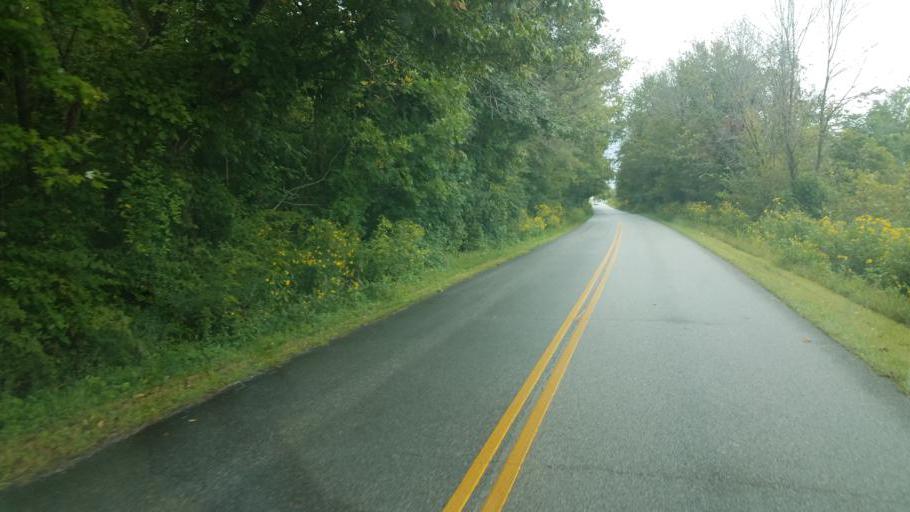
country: US
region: Ohio
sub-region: Scioto County
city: Wheelersburg
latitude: 38.7253
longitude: -82.8614
